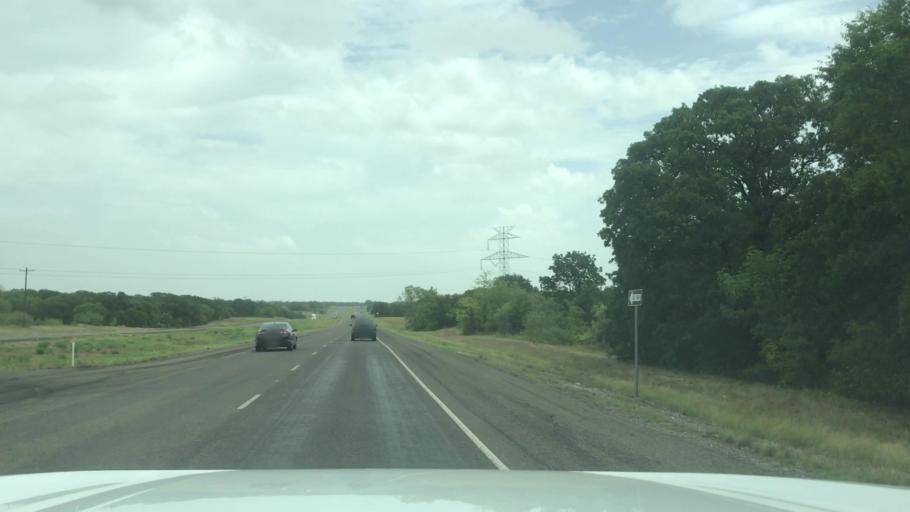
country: US
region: Texas
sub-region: McLennan County
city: Riesel
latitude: 31.5074
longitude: -96.9481
